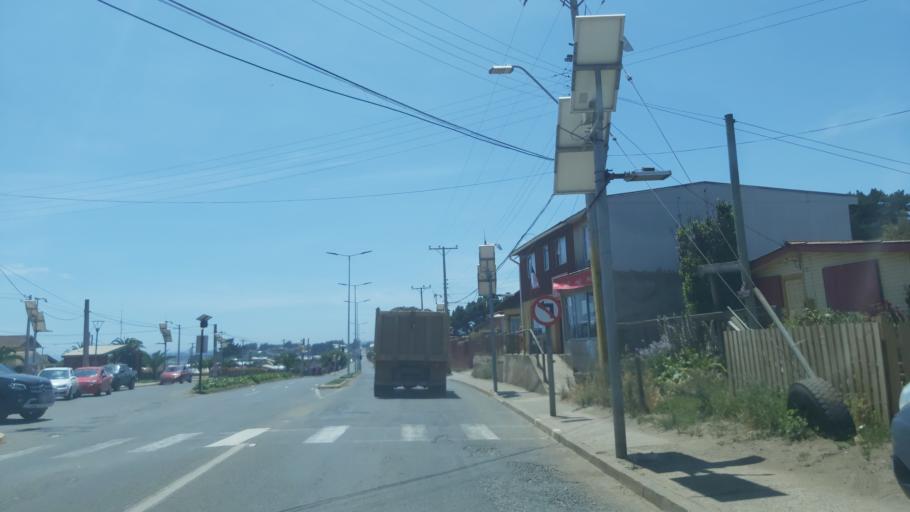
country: CL
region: Maule
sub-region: Provincia de Cauquenes
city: Cauquenes
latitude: -35.8126
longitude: -72.5731
